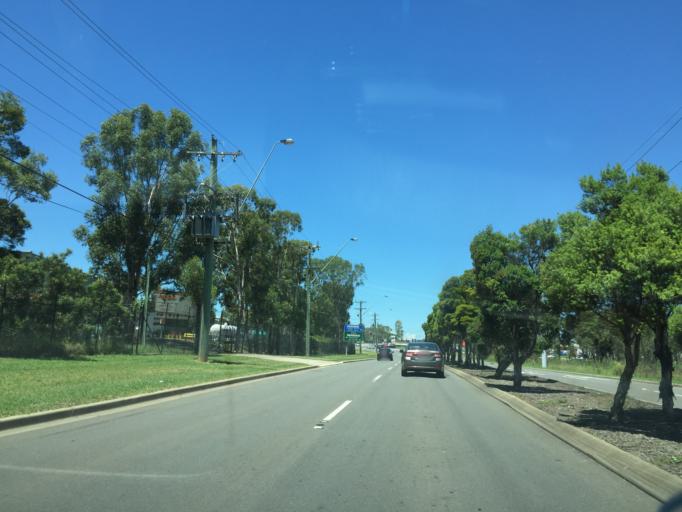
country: AU
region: New South Wales
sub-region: Blacktown
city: Doonside
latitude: -33.7901
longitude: 150.8716
